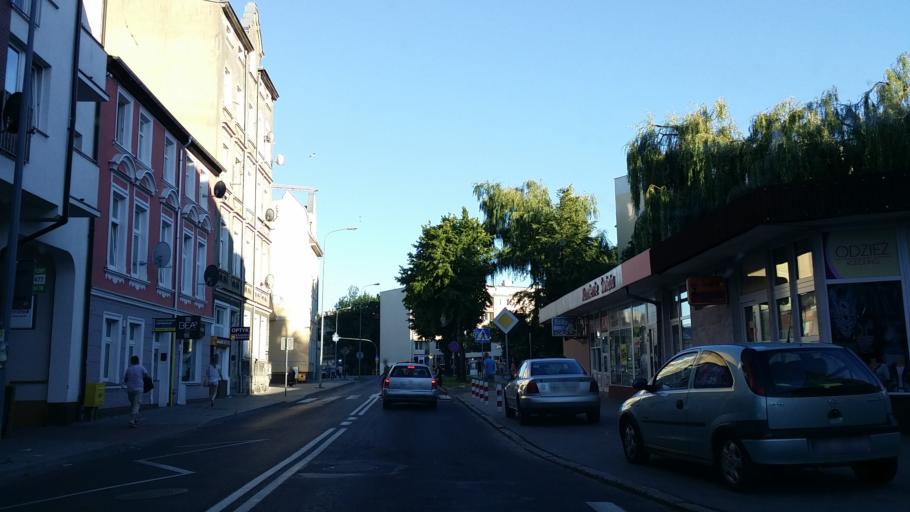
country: PL
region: West Pomeranian Voivodeship
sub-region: Powiat kolobrzeski
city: Kolobrzeg
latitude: 54.1810
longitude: 15.5754
